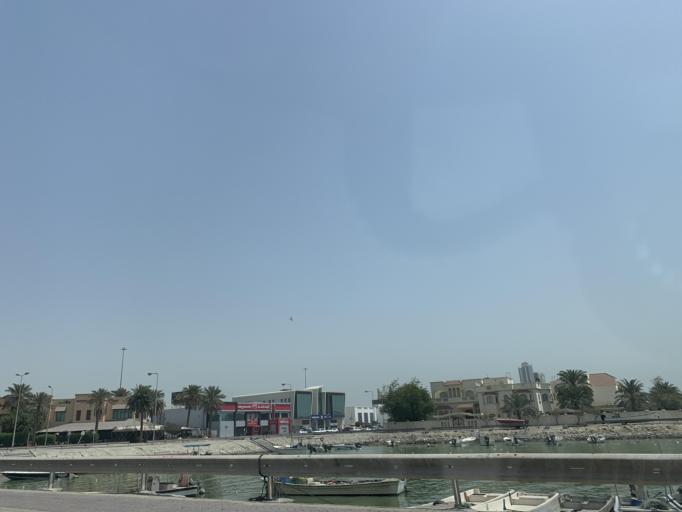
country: BH
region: Manama
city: Manama
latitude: 26.2023
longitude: 50.5673
